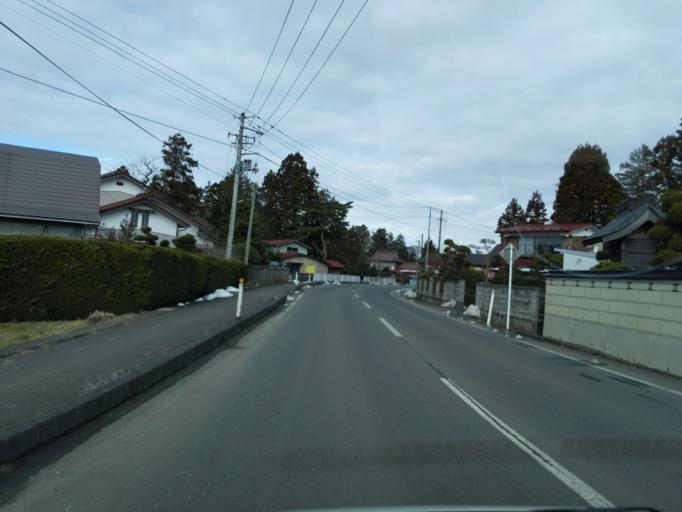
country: JP
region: Iwate
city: Mizusawa
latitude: 39.0722
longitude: 141.1637
